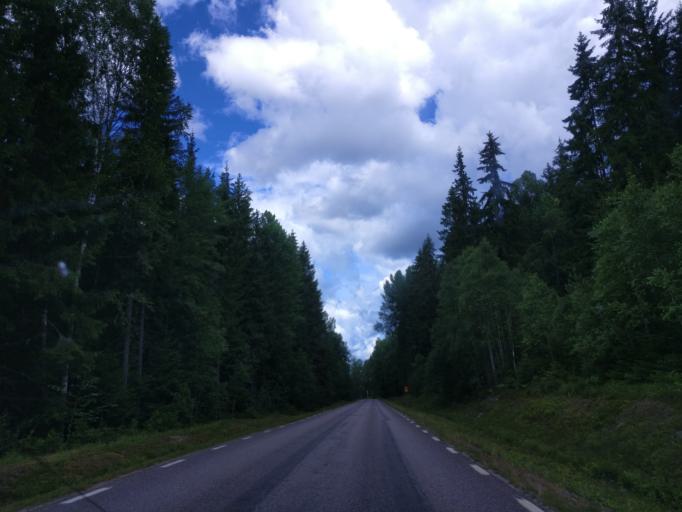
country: SE
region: Vaermland
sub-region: Hagfors Kommun
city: Ekshaerad
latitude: 60.0427
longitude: 13.5313
